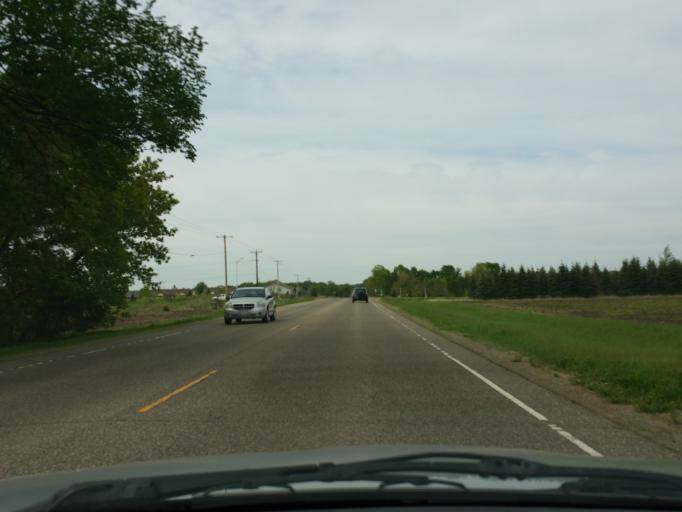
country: US
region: Wisconsin
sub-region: Saint Croix County
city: Hudson
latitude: 44.9472
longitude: -92.6906
